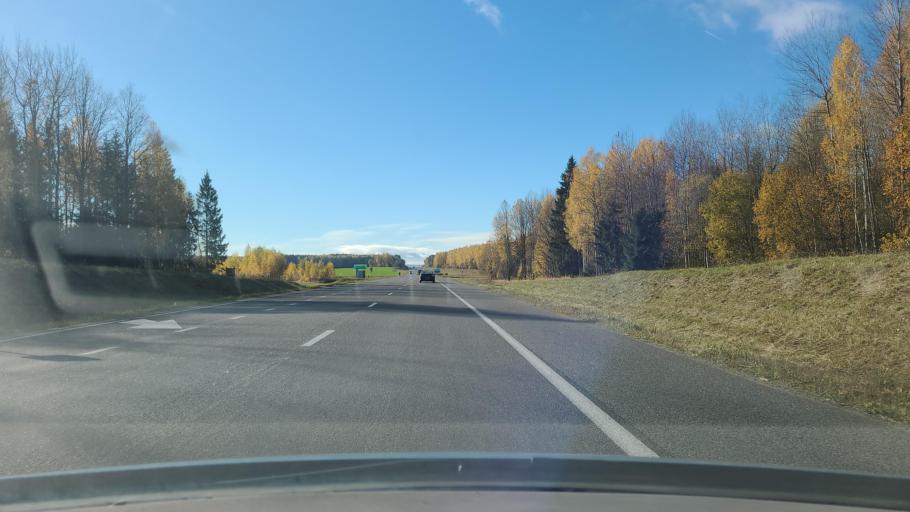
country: BY
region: Grodnenskaya
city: Astravyets
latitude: 54.6562
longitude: 26.0454
